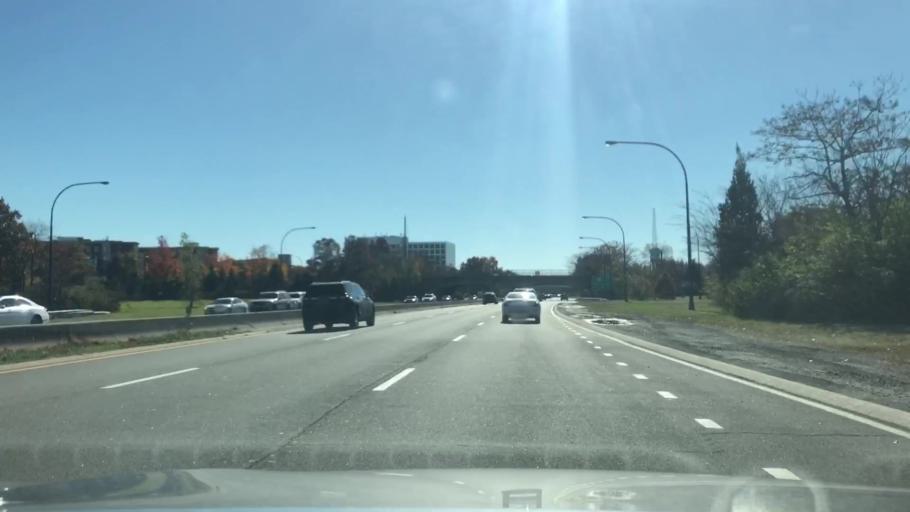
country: US
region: New York
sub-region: Nassau County
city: East Garden City
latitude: 40.7242
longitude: -73.5806
